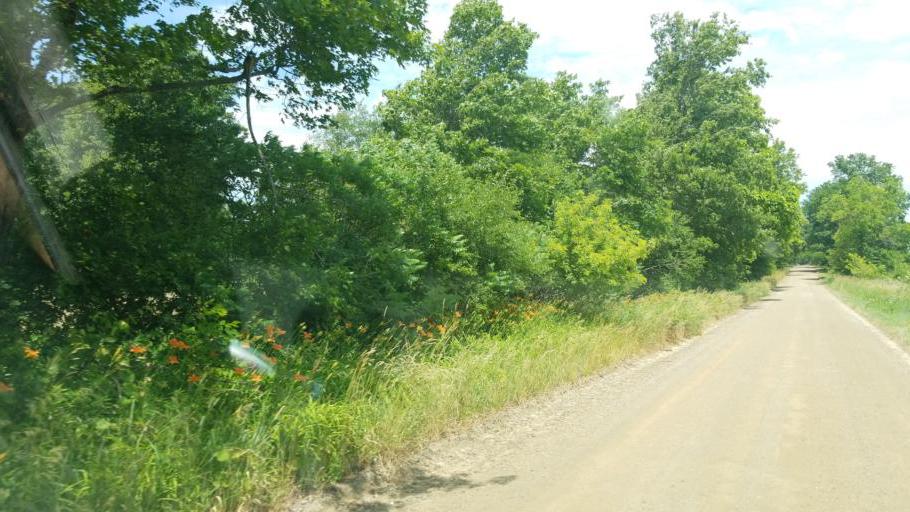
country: US
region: Michigan
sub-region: Eaton County
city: Charlotte
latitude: 42.6157
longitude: -84.8853
